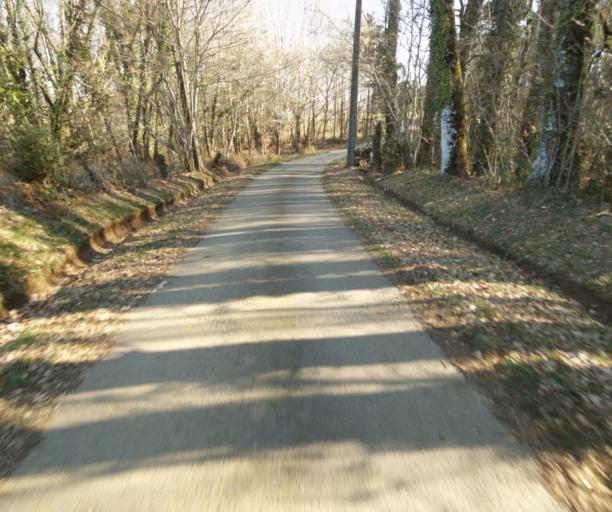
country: FR
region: Limousin
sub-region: Departement de la Correze
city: Saint-Clement
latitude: 45.3737
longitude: 1.6445
